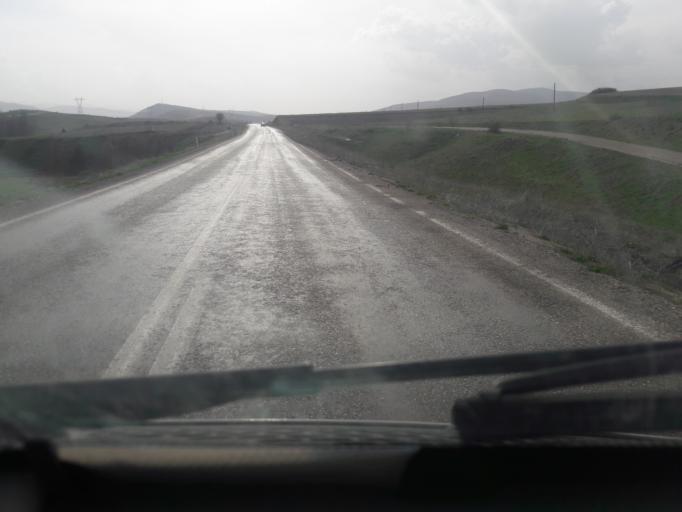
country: TR
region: Gumushane
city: Kelkit
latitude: 40.1259
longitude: 39.3493
